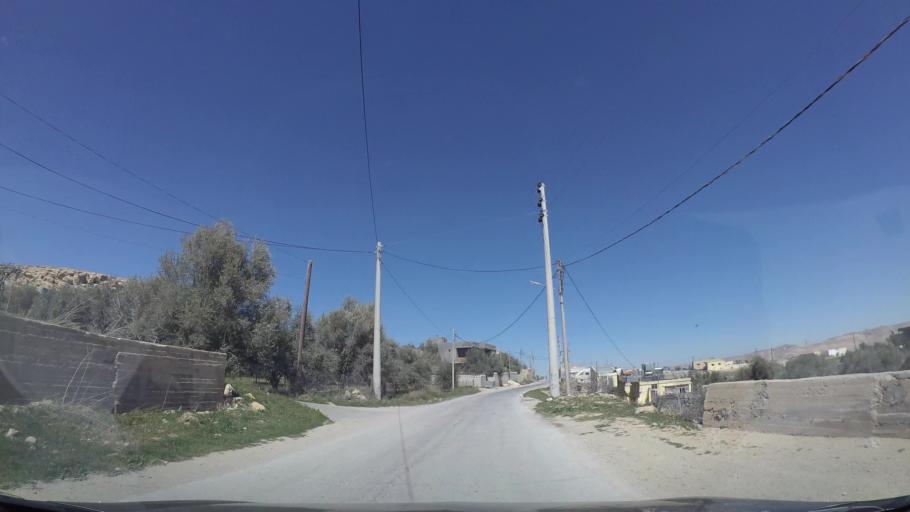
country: JO
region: Tafielah
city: At Tafilah
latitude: 30.8266
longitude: 35.5800
